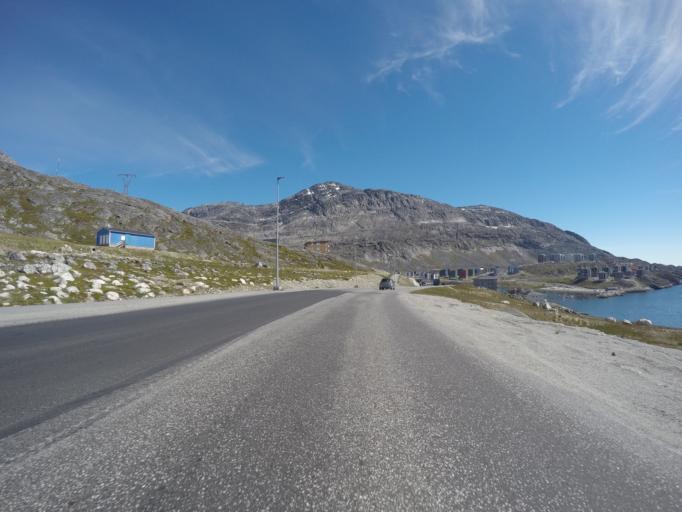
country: GL
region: Sermersooq
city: Nuuk
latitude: 64.1762
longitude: -51.6773
